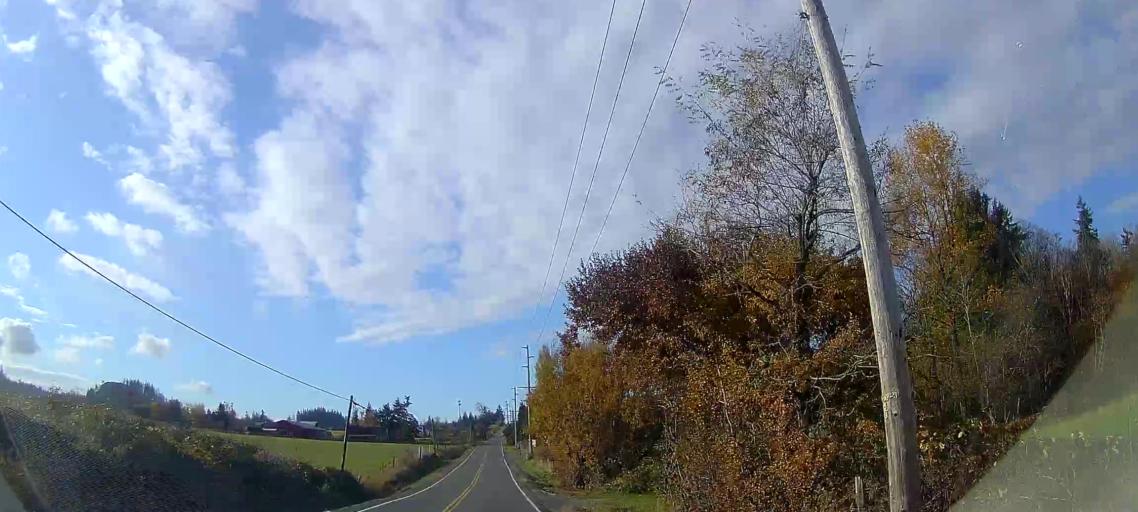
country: US
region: Washington
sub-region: Skagit County
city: Clear Lake
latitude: 48.4352
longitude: -122.2434
